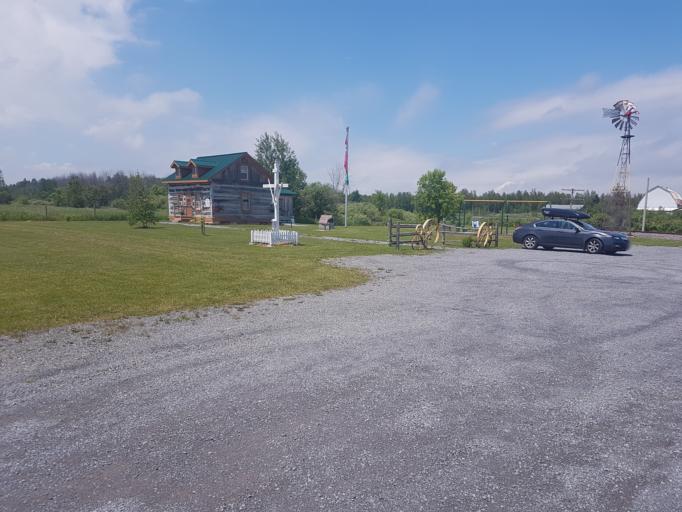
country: CA
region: Ontario
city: Bourget
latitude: 45.3285
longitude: -75.2061
